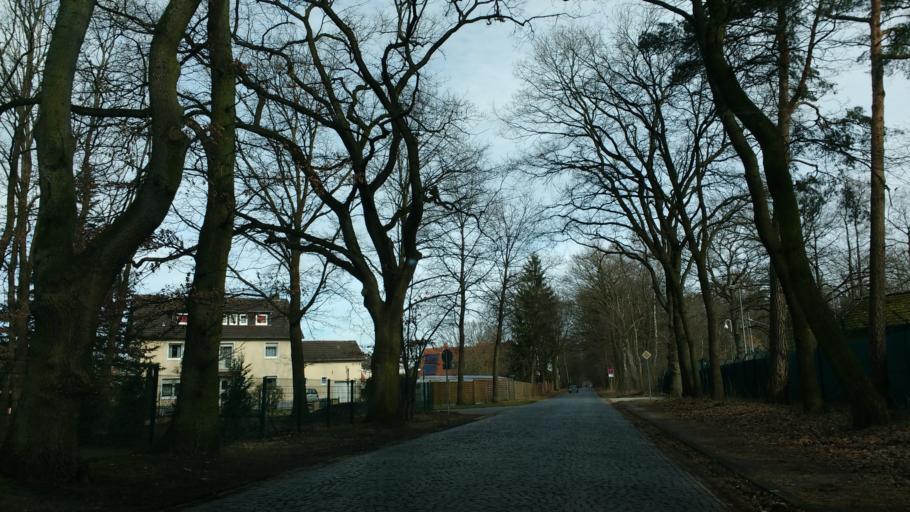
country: DE
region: North Rhine-Westphalia
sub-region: Regierungsbezirk Detmold
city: Paderborn
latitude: 51.7780
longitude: 8.7190
